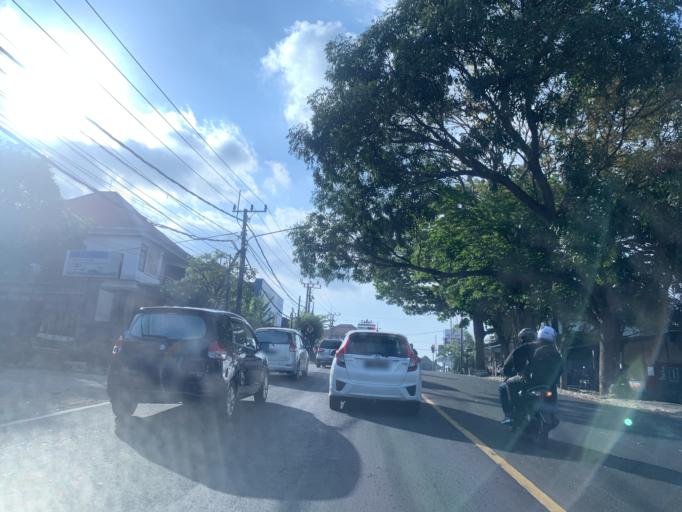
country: ID
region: Bali
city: Banjar Tegal Belodan
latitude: -8.5459
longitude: 115.1158
